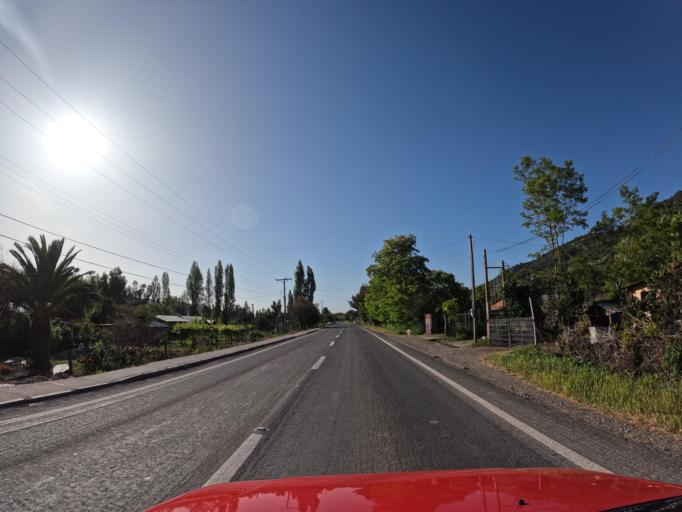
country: CL
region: Maule
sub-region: Provincia de Curico
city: Teno
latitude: -34.7949
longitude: -71.2264
